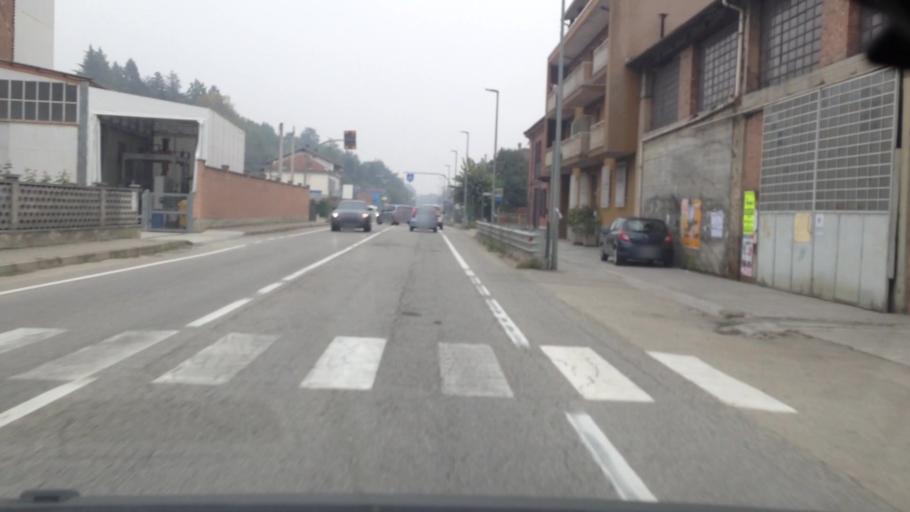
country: IT
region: Piedmont
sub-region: Provincia di Asti
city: Castello di Annone
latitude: 44.8775
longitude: 8.3193
